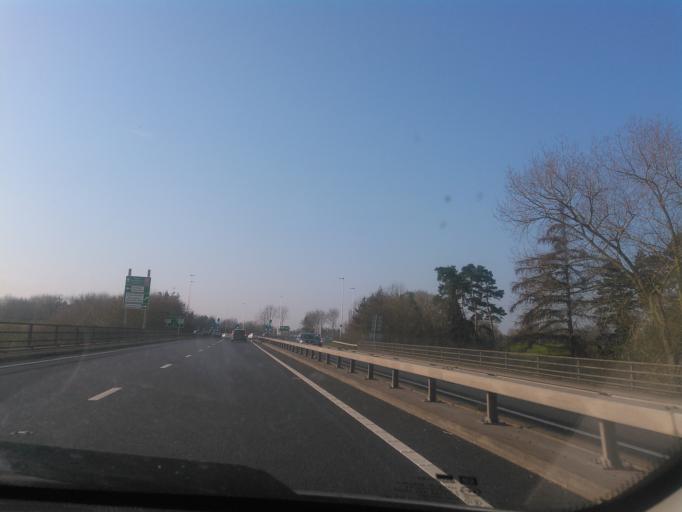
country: GB
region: England
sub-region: Shropshire
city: Berrington
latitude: 52.6942
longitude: -2.7093
